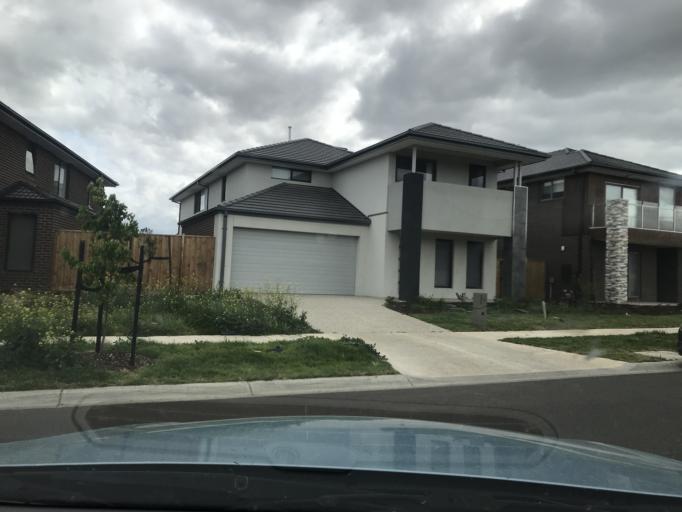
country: AU
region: Victoria
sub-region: Wyndham
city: Williams Landing
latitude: -37.8621
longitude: 144.7552
